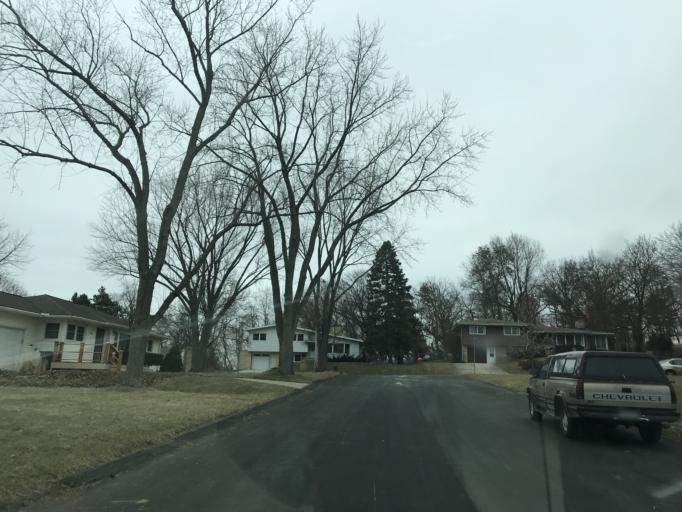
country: US
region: Wisconsin
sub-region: Dane County
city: Monona
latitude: 43.0578
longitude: -89.3220
